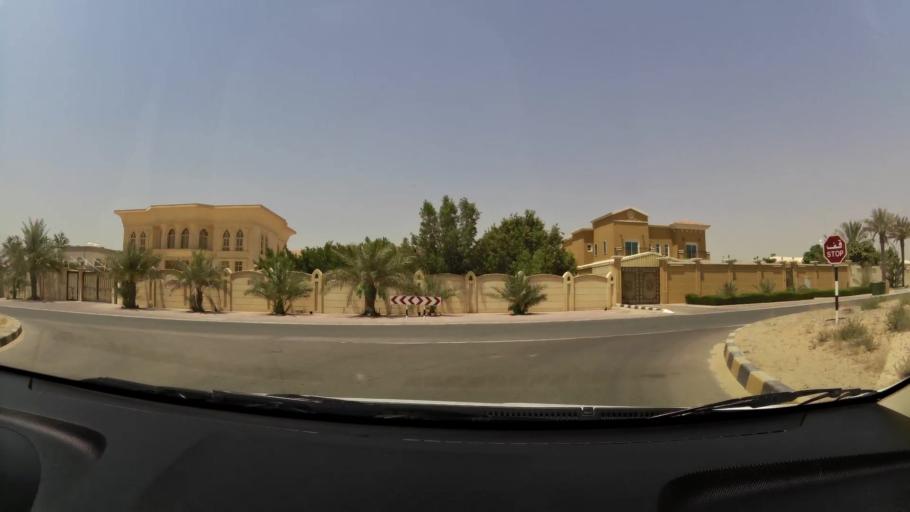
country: AE
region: Ajman
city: Ajman
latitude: 25.4189
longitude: 55.5113
